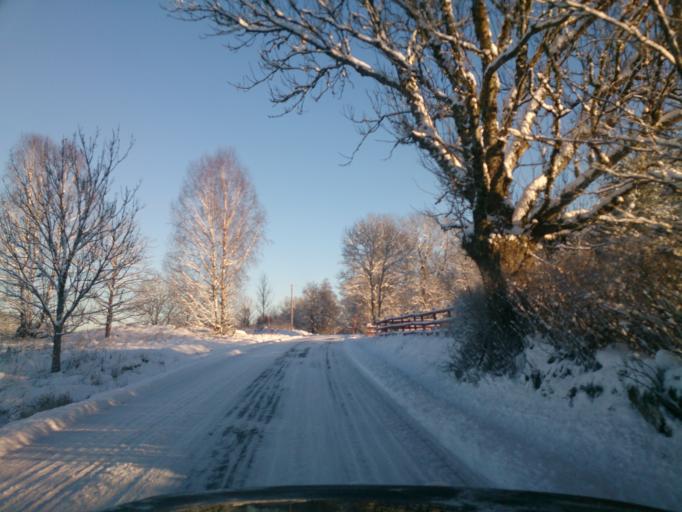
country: SE
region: OEstergoetland
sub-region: Norrkopings Kommun
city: Krokek
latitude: 58.4985
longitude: 16.5705
